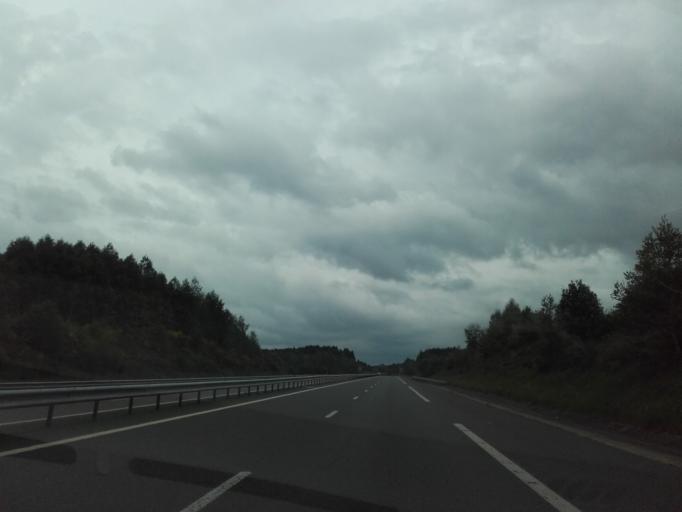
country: FR
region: Auvergne
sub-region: Departement du Puy-de-Dome
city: Saint-Sauves-d'Auvergne
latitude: 45.6409
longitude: 2.5809
